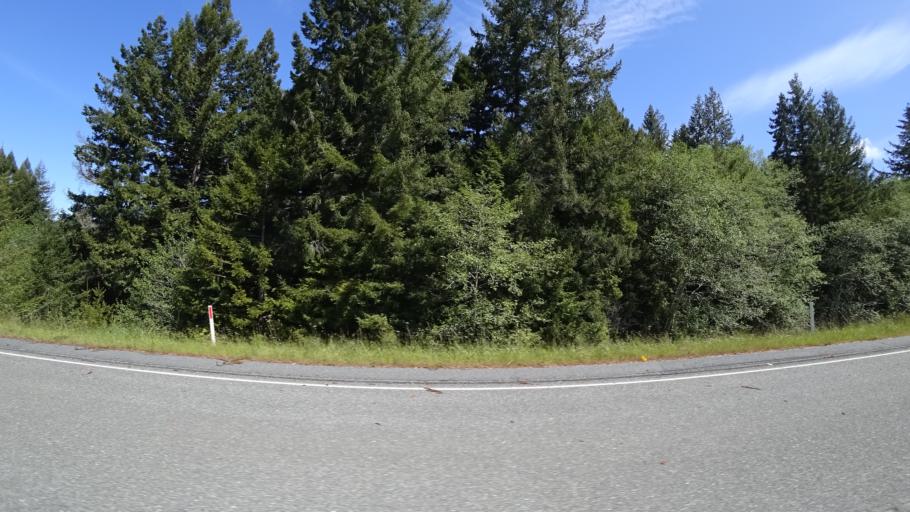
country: US
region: California
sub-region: Humboldt County
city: Westhaven-Moonstone
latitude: 41.3590
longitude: -123.9980
